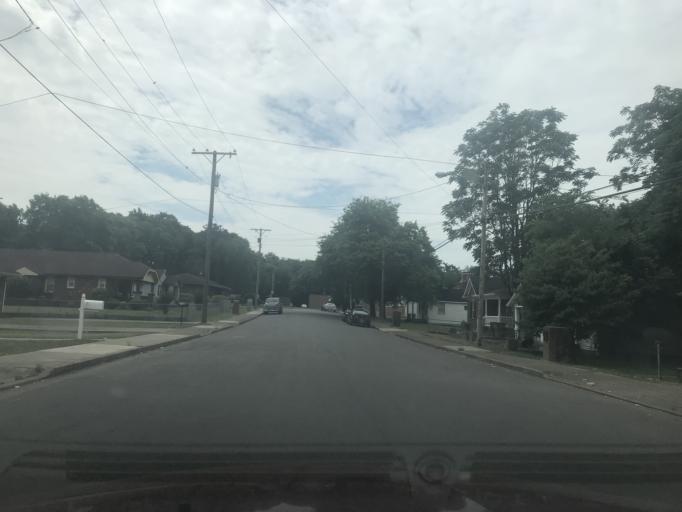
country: US
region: Tennessee
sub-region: Davidson County
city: Nashville
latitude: 36.1717
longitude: -86.8113
